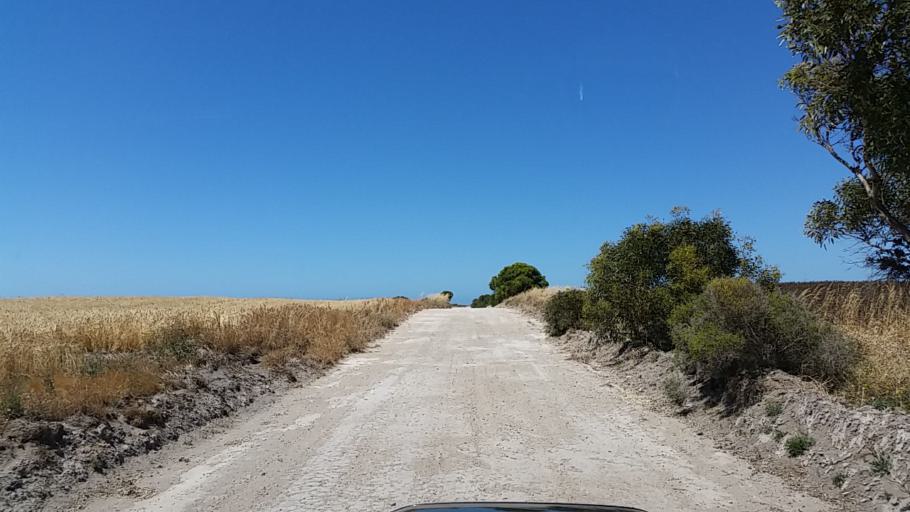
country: AU
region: South Australia
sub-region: Yorke Peninsula
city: Honiton
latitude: -35.2339
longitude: 137.1256
